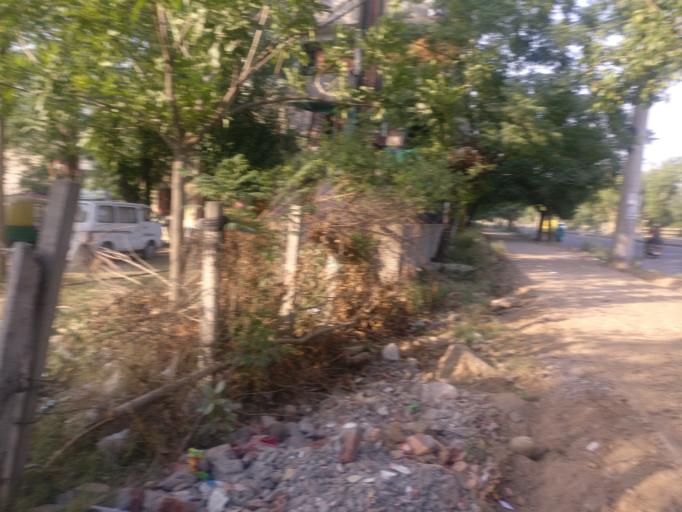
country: IN
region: Punjab
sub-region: Ajitgarh
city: Mohali
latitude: 30.7339
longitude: 76.7212
